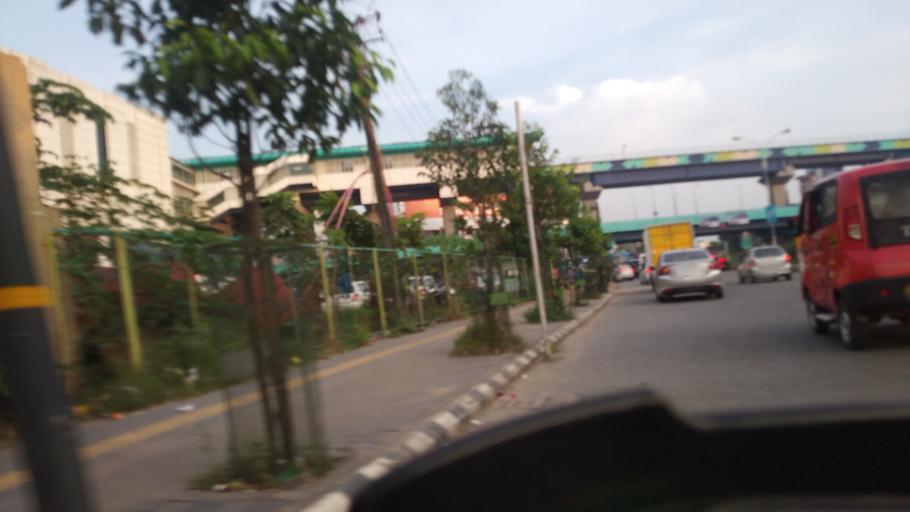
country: IN
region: Kerala
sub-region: Ernakulam
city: Elur
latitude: 10.0255
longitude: 76.3072
